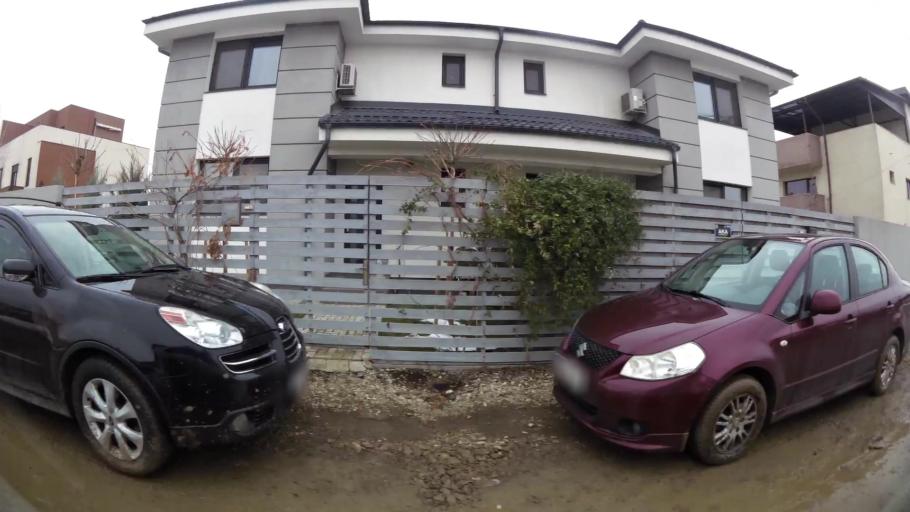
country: RO
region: Ilfov
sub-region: Comuna Otopeni
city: Otopeni
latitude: 44.5556
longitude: 26.0984
